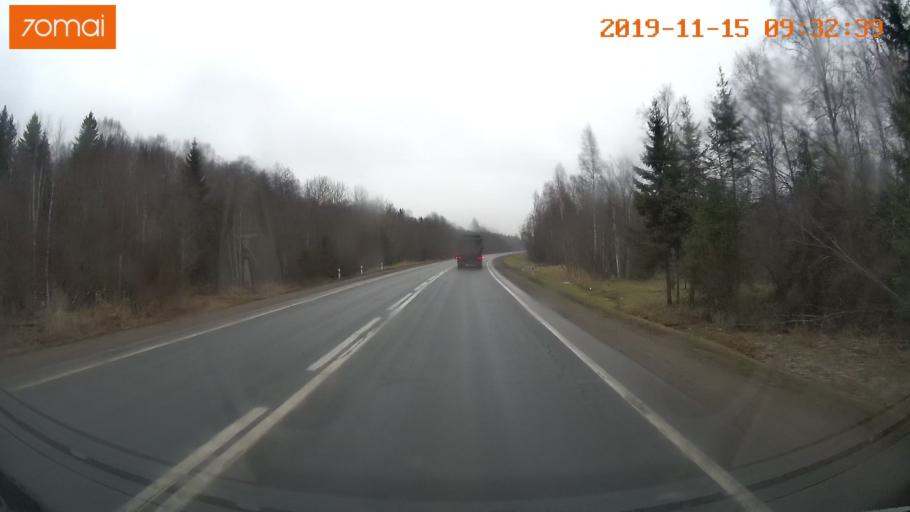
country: RU
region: Vologda
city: Sheksna
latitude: 59.2707
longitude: 38.3403
